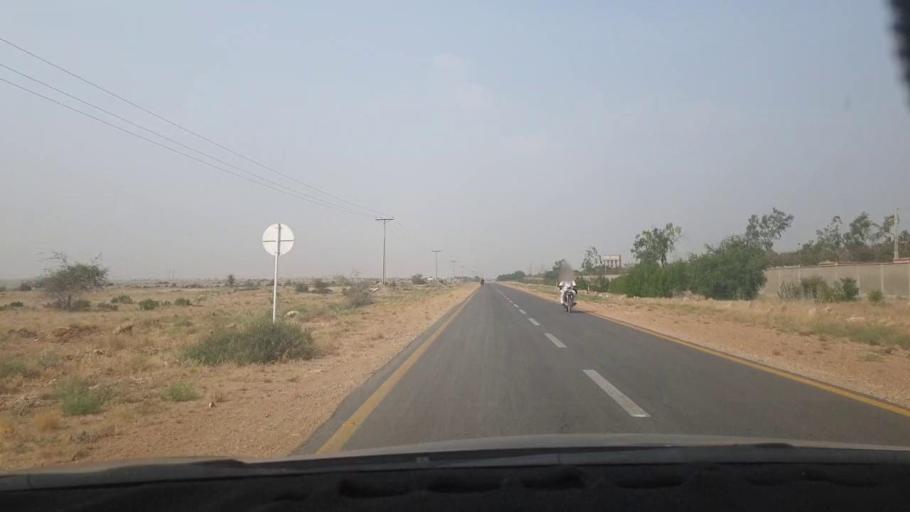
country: PK
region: Sindh
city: Jamshoro
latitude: 25.5555
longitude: 68.3199
